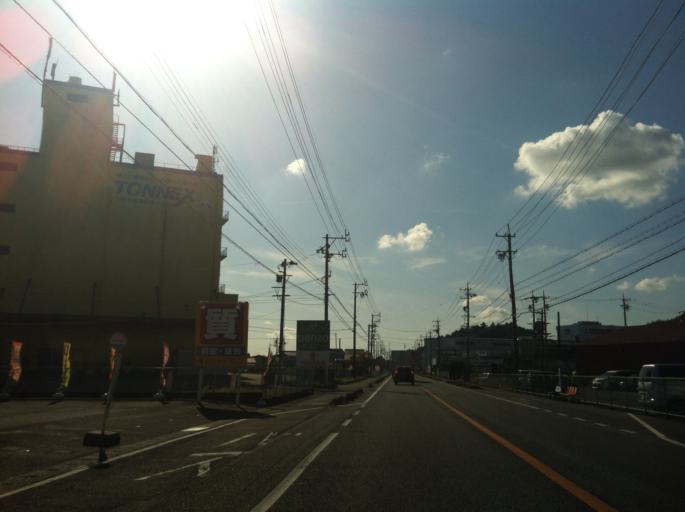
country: JP
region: Shizuoka
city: Fujieda
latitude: 34.8904
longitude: 138.2799
